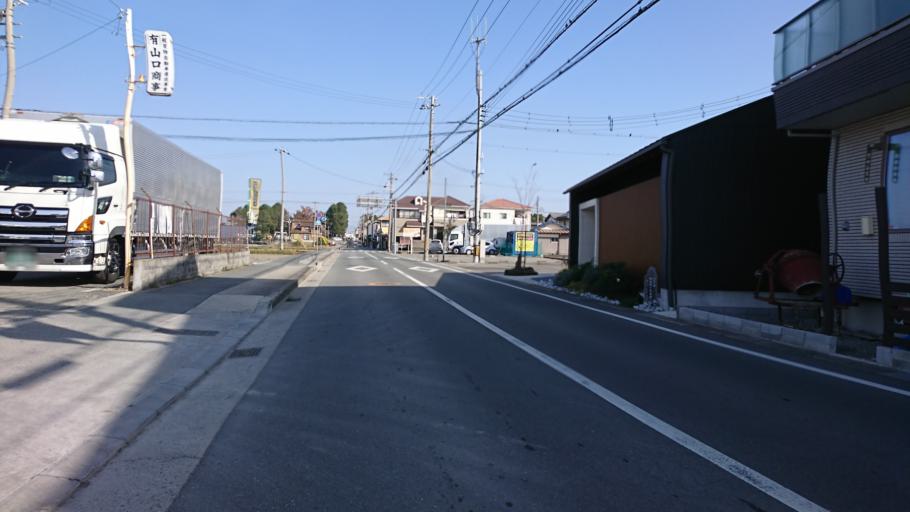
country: JP
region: Hyogo
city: Kakogawacho-honmachi
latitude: 34.7255
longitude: 134.8743
